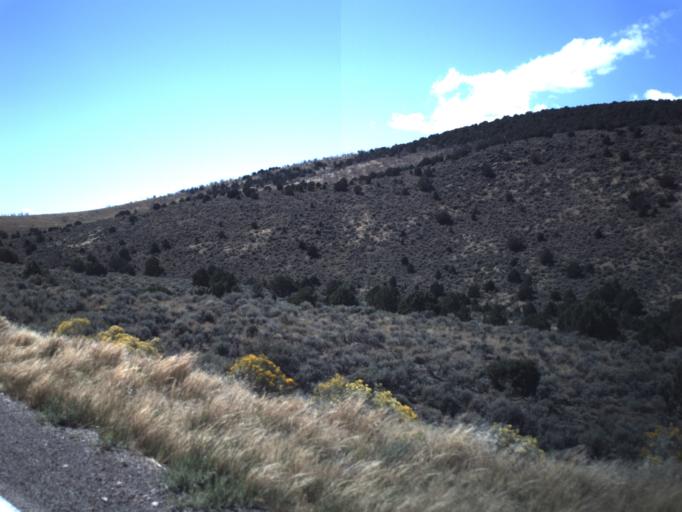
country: US
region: Utah
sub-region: Beaver County
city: Milford
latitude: 38.1167
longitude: -112.9521
